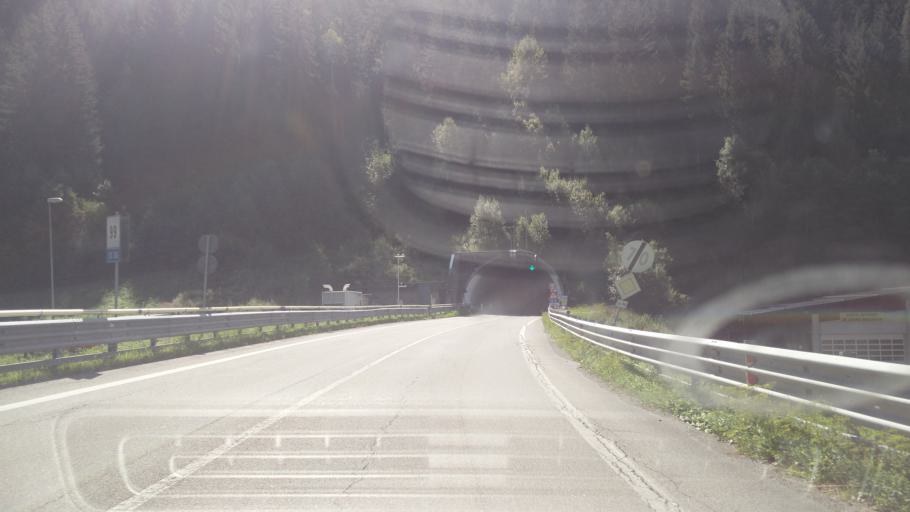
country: IT
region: Lombardy
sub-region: Provincia di Sondrio
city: Cepina
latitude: 46.4477
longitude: 10.3637
